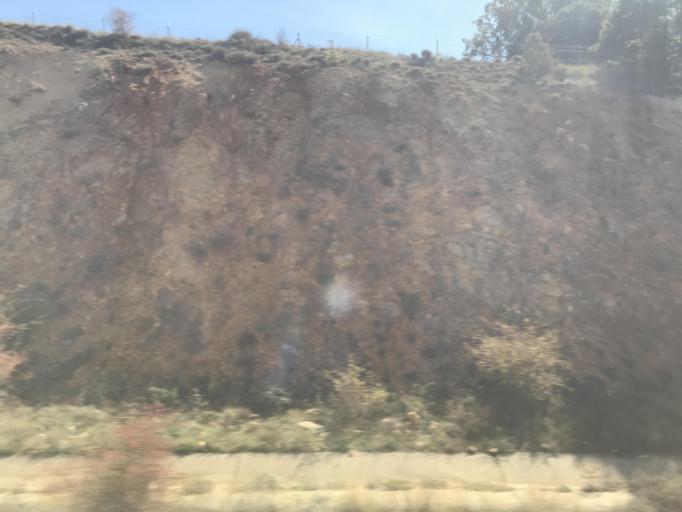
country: ES
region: Castille and Leon
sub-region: Provincia de Soria
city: Arcos de Jalon
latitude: 41.1420
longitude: -2.3181
